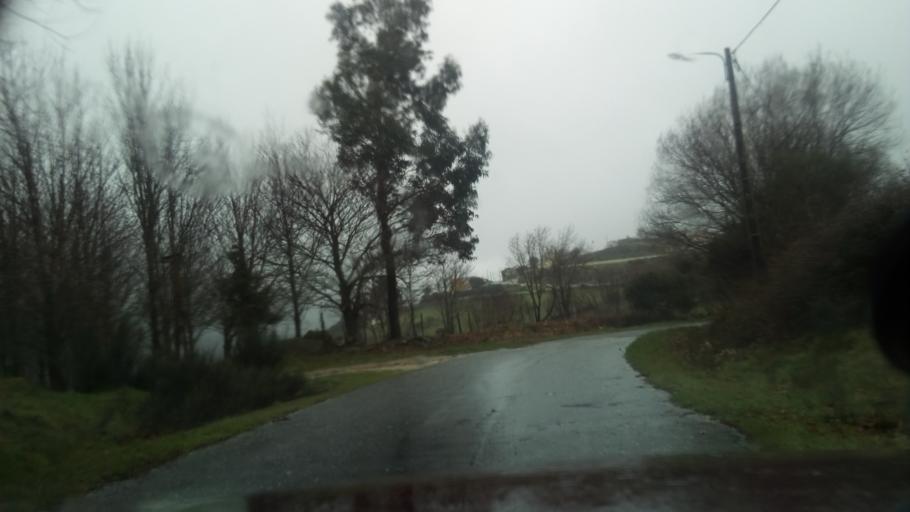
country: PT
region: Guarda
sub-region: Celorico da Beira
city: Celorico da Beira
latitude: 40.5404
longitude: -7.4543
